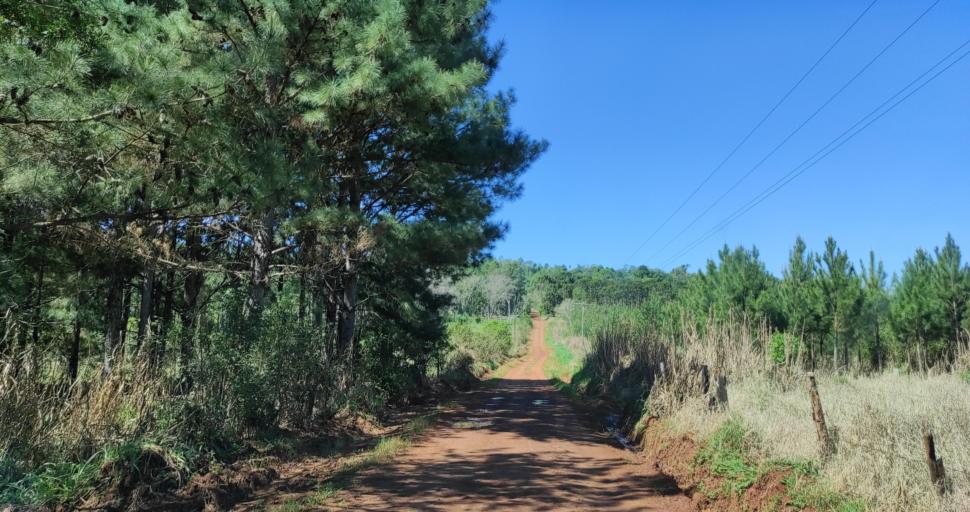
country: AR
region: Misiones
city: Capiovi
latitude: -26.9346
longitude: -54.9969
